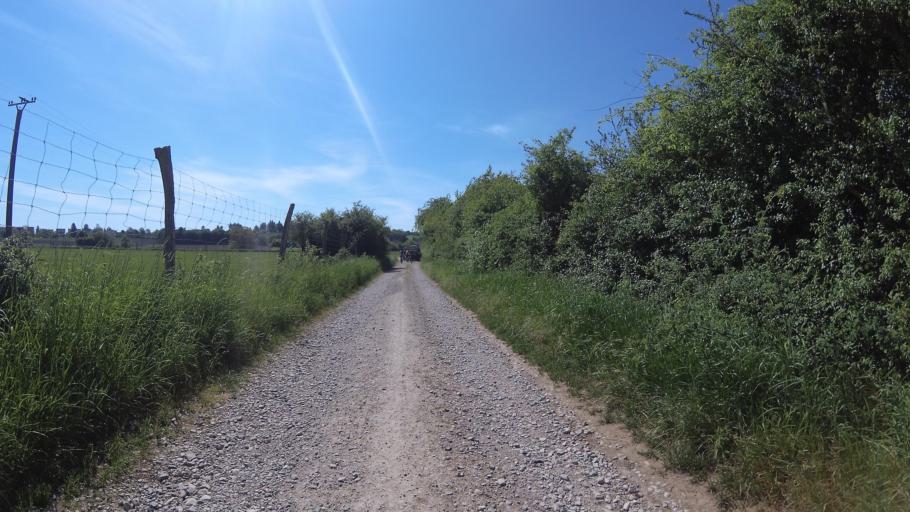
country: DE
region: Saarland
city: Blieskastel
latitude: 49.2205
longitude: 7.1923
